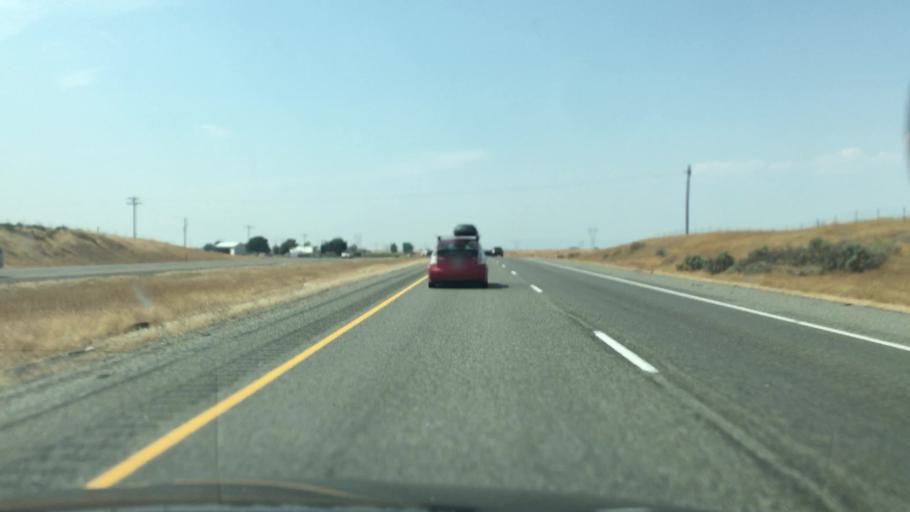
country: US
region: Idaho
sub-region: Gooding County
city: Wendell
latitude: 42.8301
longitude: -114.8056
